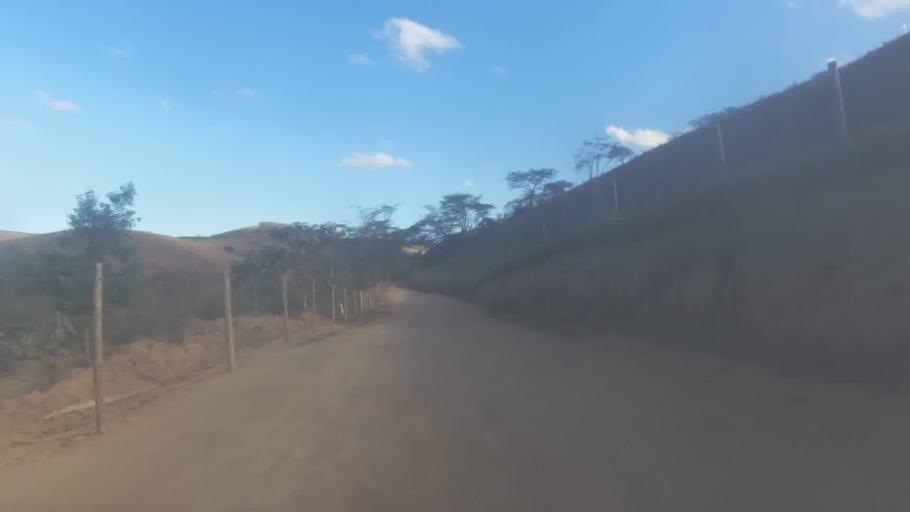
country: BR
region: Espirito Santo
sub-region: Mimoso Do Sul
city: Mimoso do Sul
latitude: -21.0790
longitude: -41.1458
